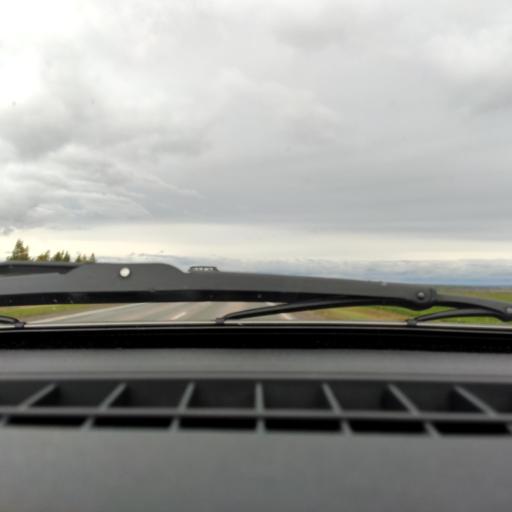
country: RU
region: Bashkortostan
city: Rayevskiy
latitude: 54.1099
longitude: 54.9247
